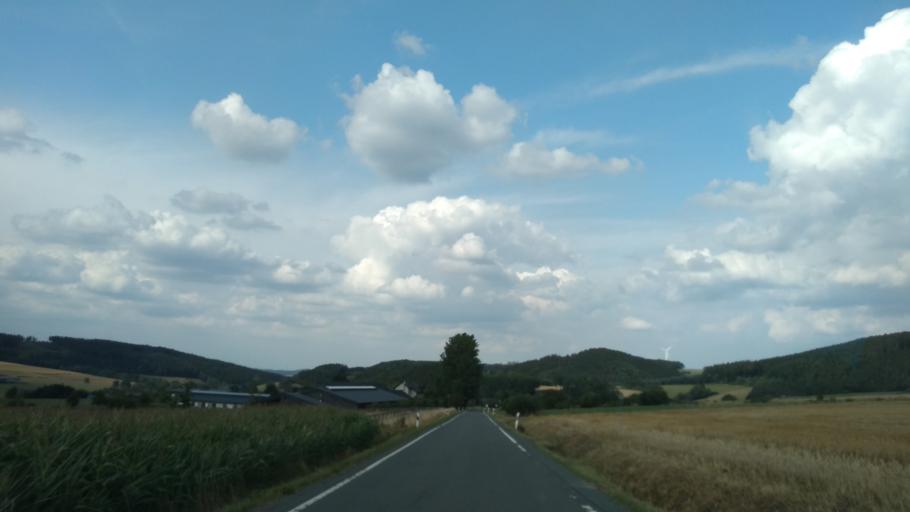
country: DE
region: North Rhine-Westphalia
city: Plettenberg
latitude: 51.2660
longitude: 7.8724
